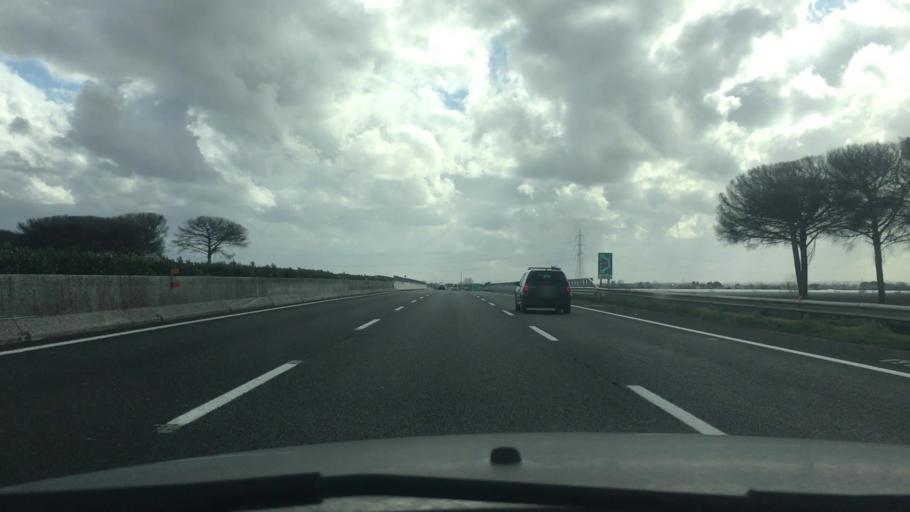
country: IT
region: Campania
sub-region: Provincia di Napoli
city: Pascarola
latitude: 40.9870
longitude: 14.3250
